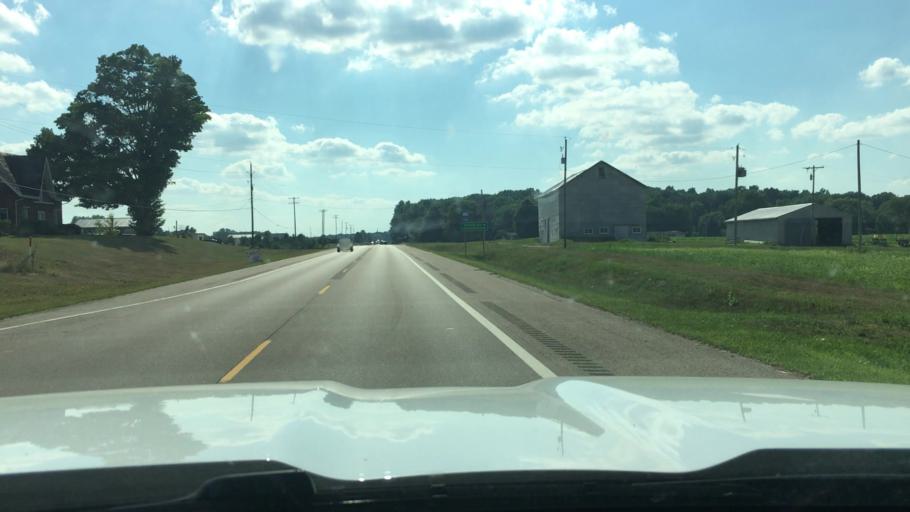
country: US
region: Michigan
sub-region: Kent County
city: Forest Hills
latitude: 43.0830
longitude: -85.3924
